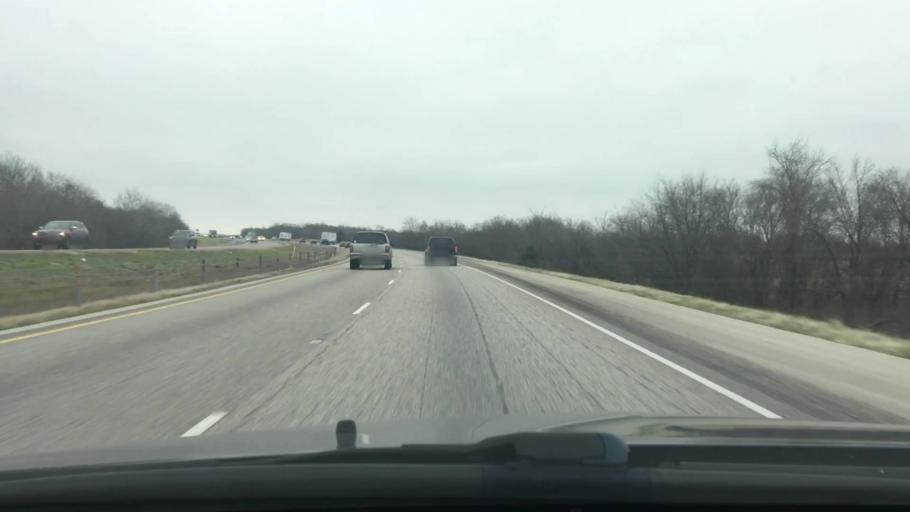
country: US
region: Texas
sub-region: Freestone County
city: Wortham
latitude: 31.8703
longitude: -96.3363
